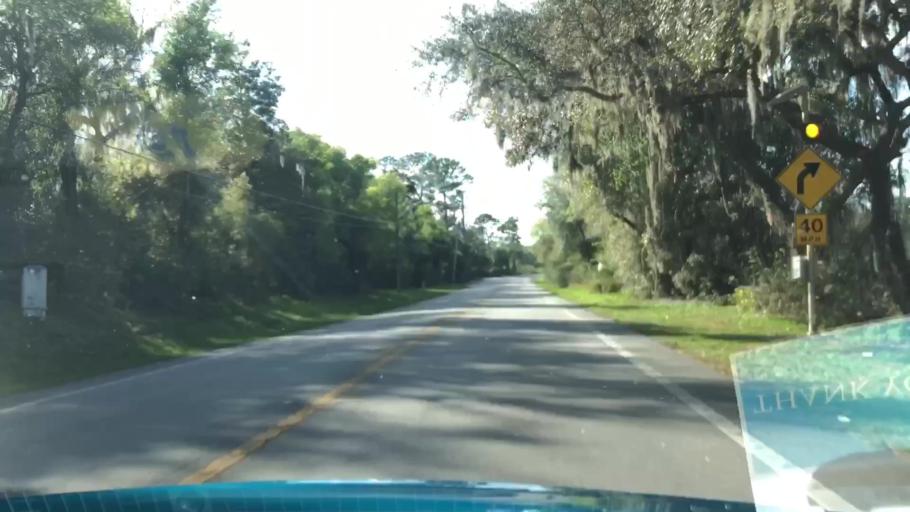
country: US
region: Florida
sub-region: Volusia County
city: Deltona
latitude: 28.8656
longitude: -81.2172
